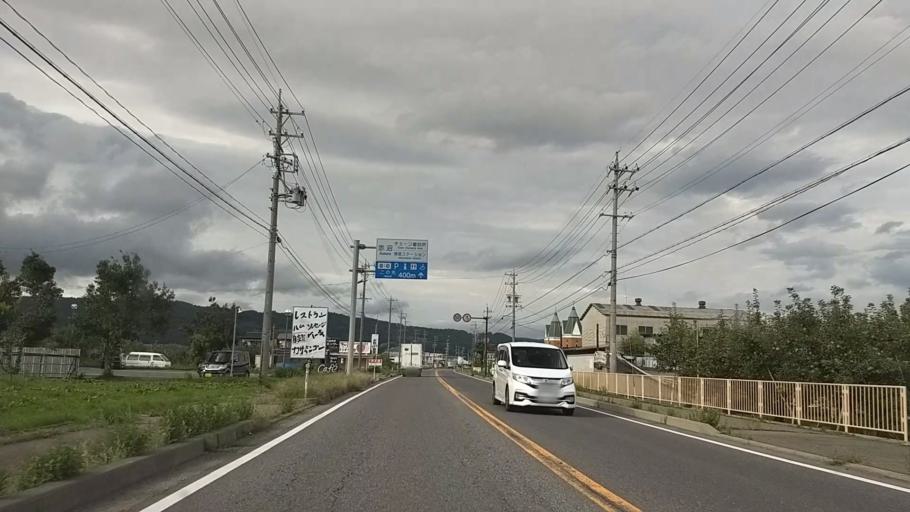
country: JP
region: Nagano
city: Suzaka
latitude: 36.6909
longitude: 138.2683
